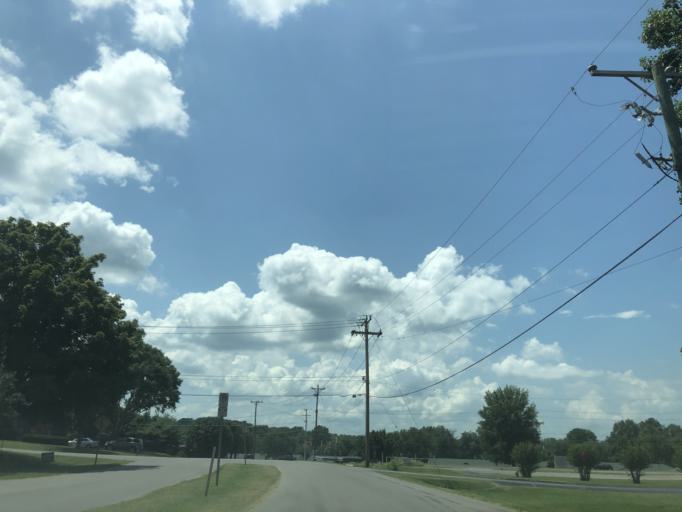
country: US
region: Tennessee
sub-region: Davidson County
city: Lakewood
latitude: 36.2042
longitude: -86.6127
